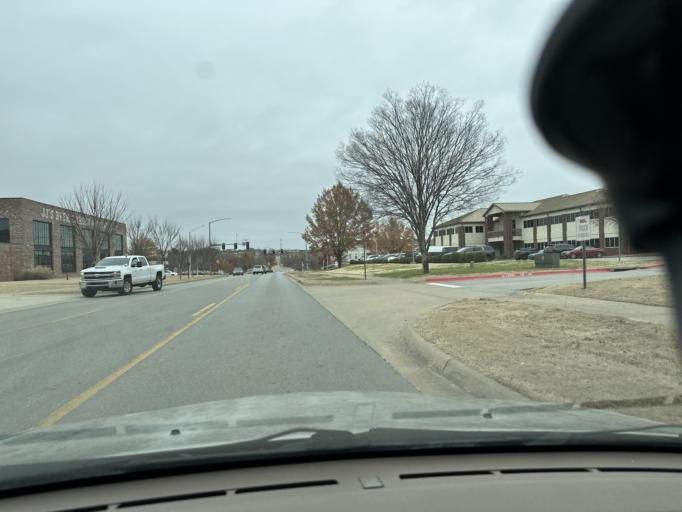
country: US
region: Arkansas
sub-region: Washington County
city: Johnson
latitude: 36.1166
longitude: -94.1568
